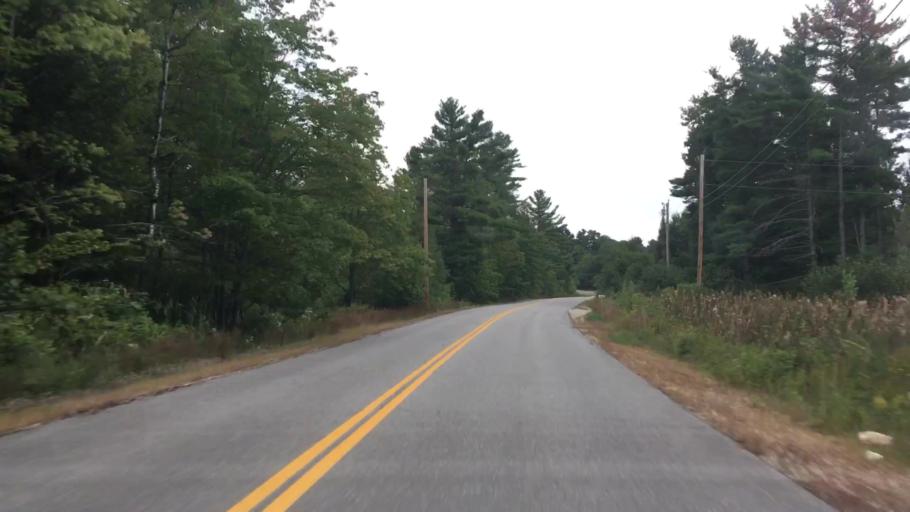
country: US
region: Maine
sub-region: Cumberland County
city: New Gloucester
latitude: 43.9034
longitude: -70.2092
